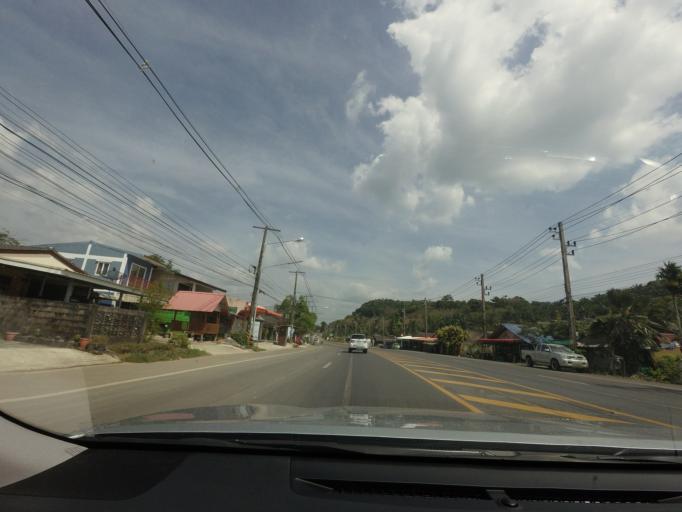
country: TH
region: Phangnga
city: Ban Ao Nang
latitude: 8.0524
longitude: 98.7652
